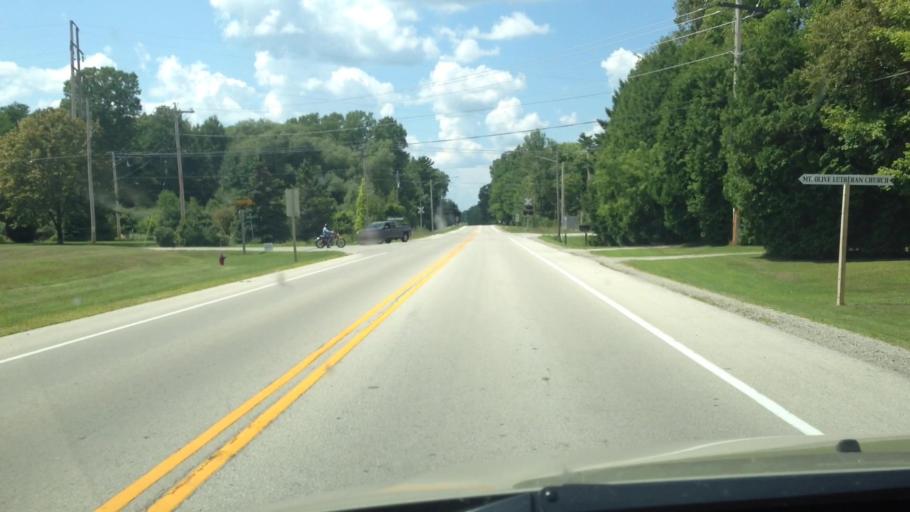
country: US
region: Wisconsin
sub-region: Brown County
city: Suamico
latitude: 44.6380
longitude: -88.0687
